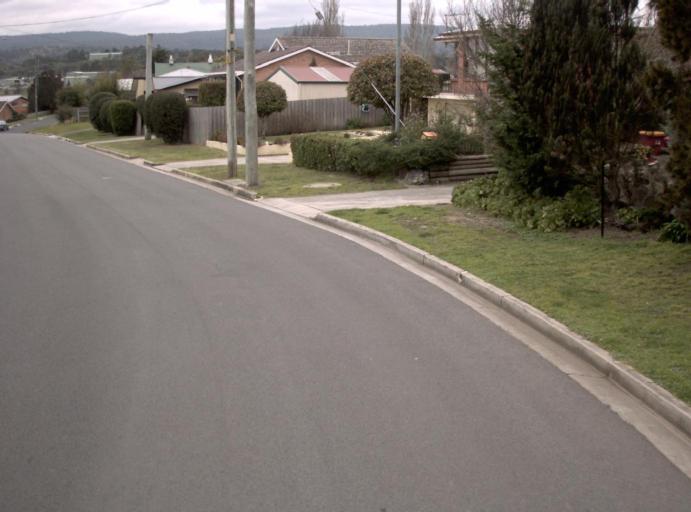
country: AU
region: Tasmania
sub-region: Launceston
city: Newstead
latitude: -41.4491
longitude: 147.1776
